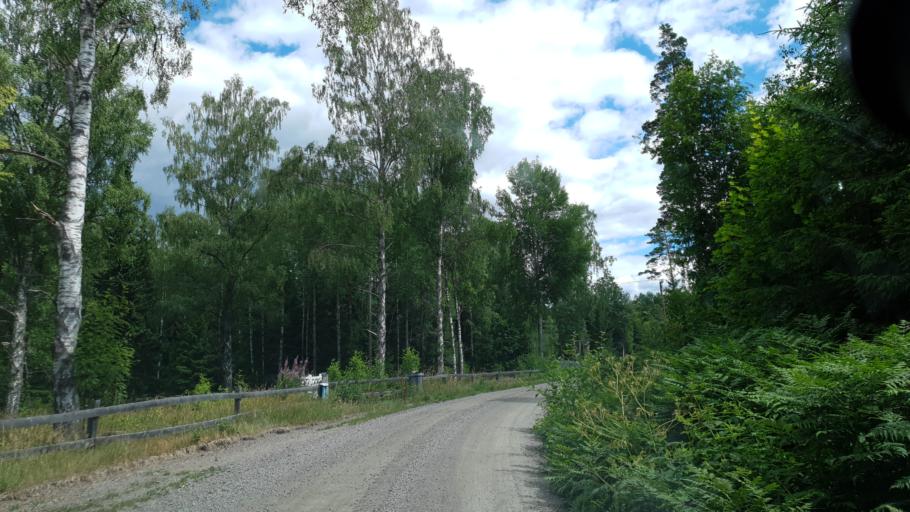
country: SE
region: Kalmar
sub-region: Hultsfreds Kommun
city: Virserum
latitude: 57.0939
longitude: 15.6323
